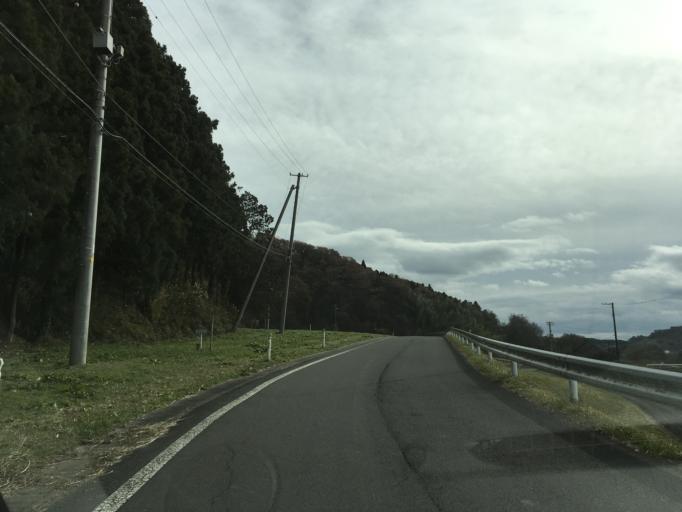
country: JP
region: Iwate
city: Ichinoseki
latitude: 38.7676
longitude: 141.2733
